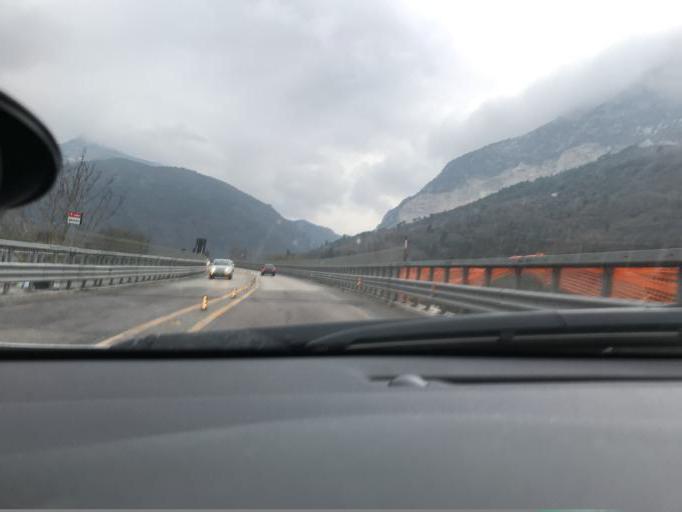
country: IT
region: The Marches
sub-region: Provincia di Ancona
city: Serra San Quirico
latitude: 43.4387
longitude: 13.0233
